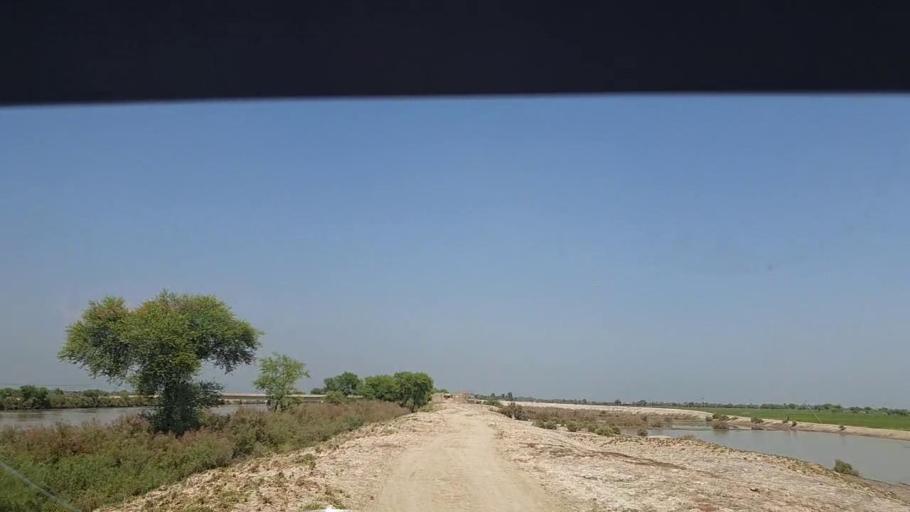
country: PK
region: Sindh
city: Kandhkot
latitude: 28.1872
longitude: 69.1601
